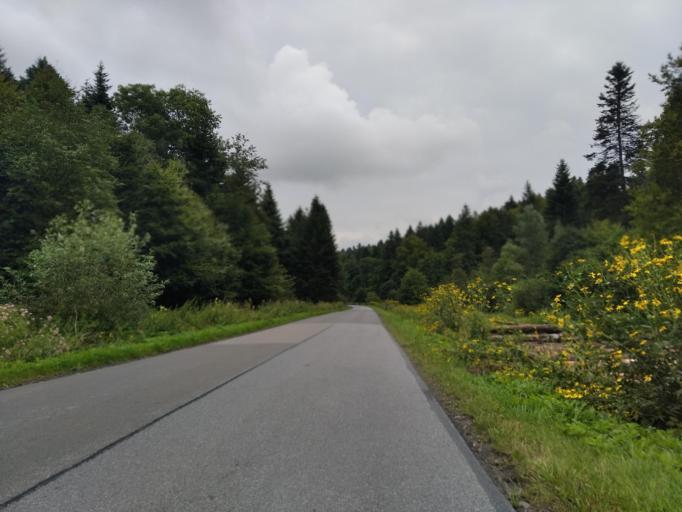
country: PL
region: Subcarpathian Voivodeship
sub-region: Powiat sanocki
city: Tyrawa Woloska
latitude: 49.6986
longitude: 22.3476
